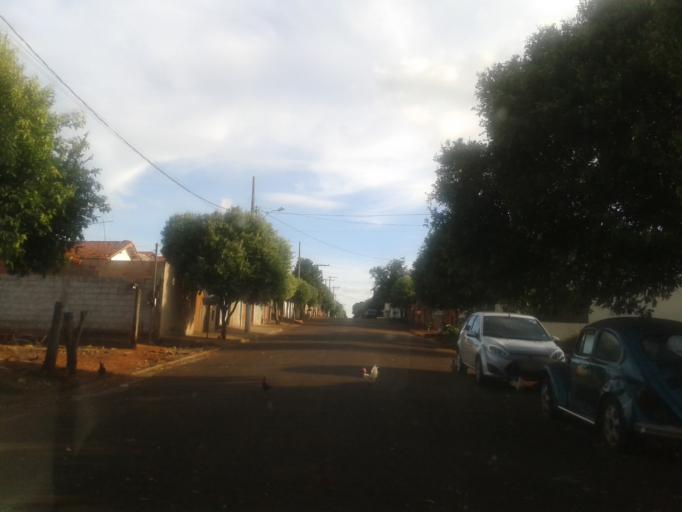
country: BR
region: Minas Gerais
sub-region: Capinopolis
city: Capinopolis
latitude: -18.6767
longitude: -49.5672
